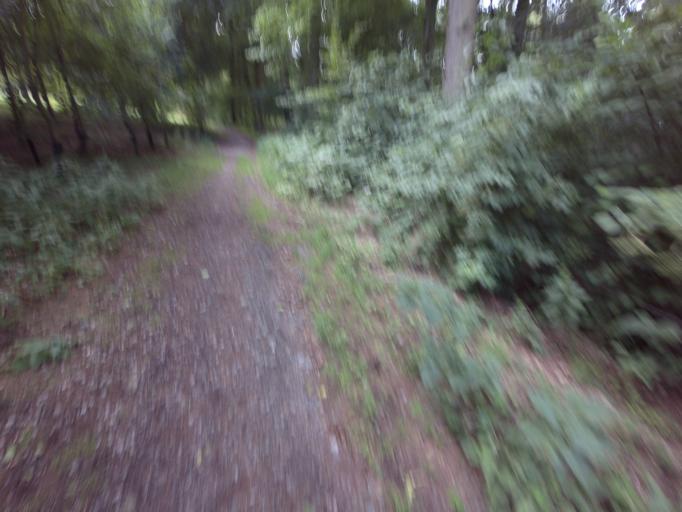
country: BE
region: Wallonia
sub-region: Province de Liege
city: La Calamine
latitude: 50.7042
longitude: 6.0174
